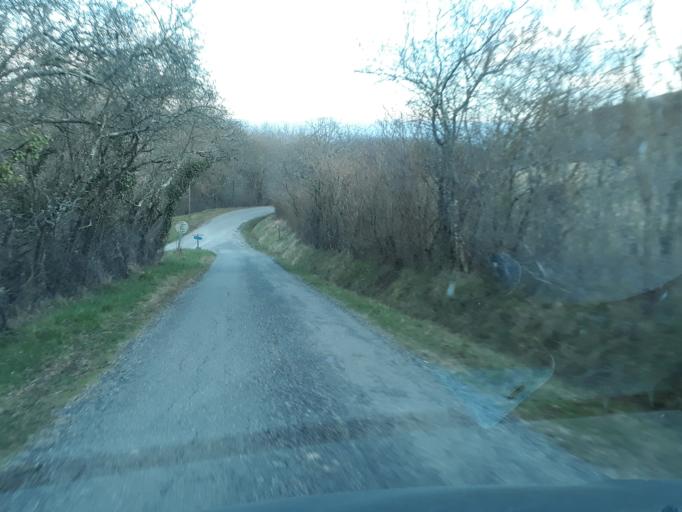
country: FR
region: Midi-Pyrenees
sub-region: Departement de la Haute-Garonne
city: Montesquieu-Volvestre
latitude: 43.1753
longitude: 1.3211
